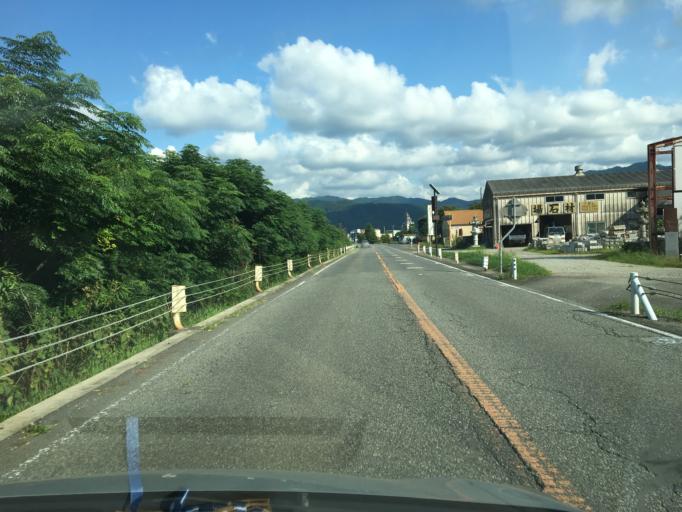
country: JP
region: Hyogo
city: Toyooka
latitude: 35.4435
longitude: 134.7762
